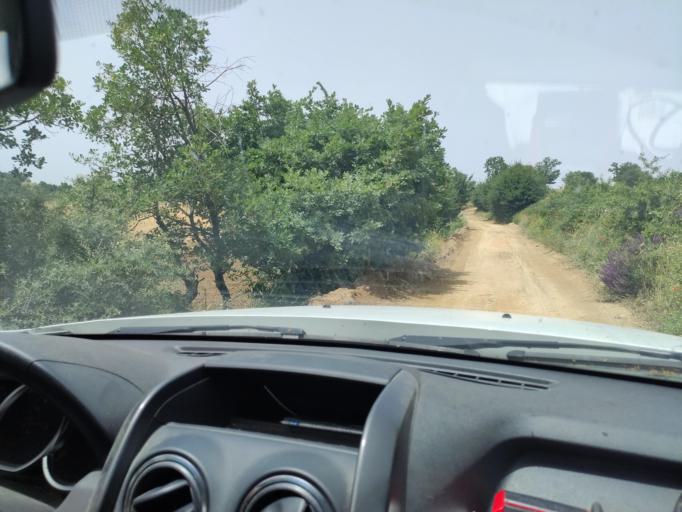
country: MK
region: Radovis
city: Radovish
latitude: 41.6757
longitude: 22.4024
